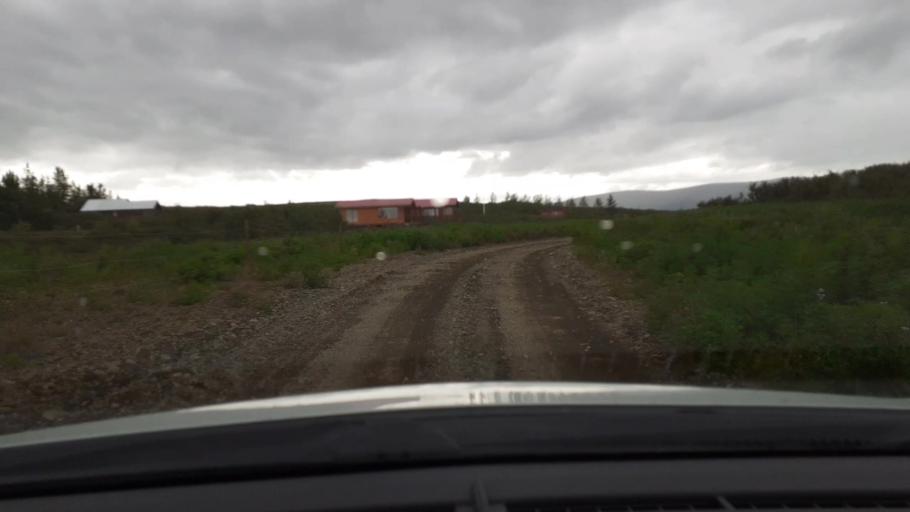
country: IS
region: West
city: Borgarnes
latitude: 64.4584
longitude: -21.9510
